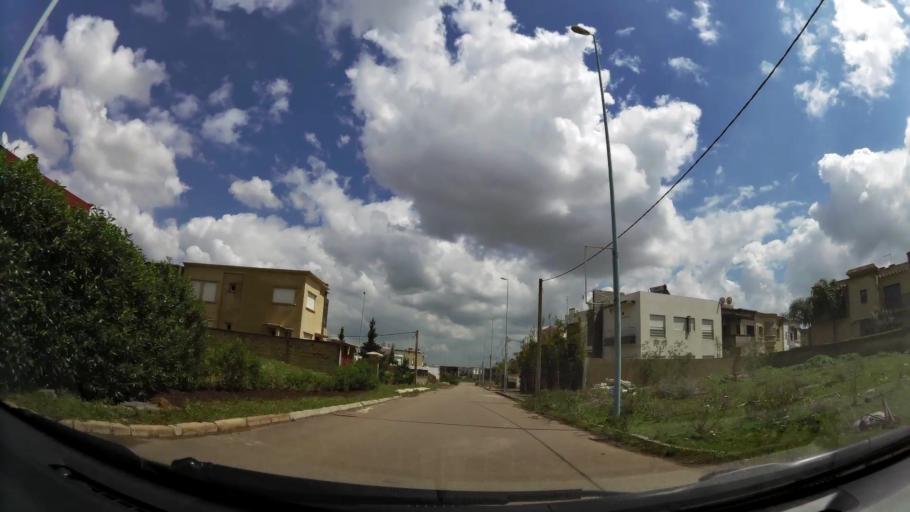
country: MA
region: Chaouia-Ouardigha
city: Nouaseur
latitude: 33.3971
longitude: -7.5654
